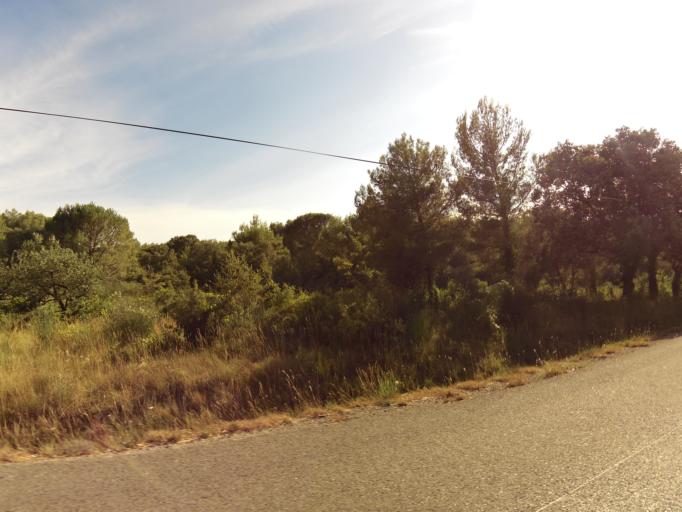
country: FR
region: Languedoc-Roussillon
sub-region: Departement du Gard
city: Caveirac
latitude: 43.8214
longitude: 4.2866
